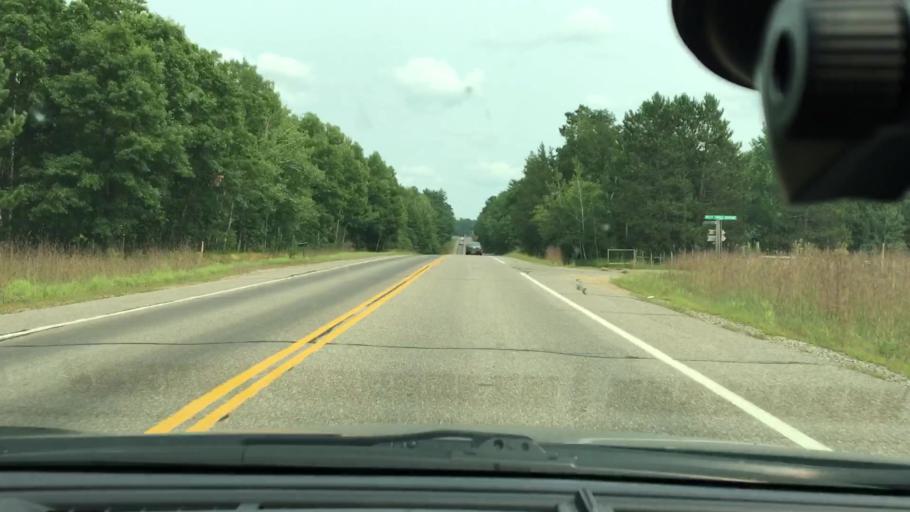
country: US
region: Minnesota
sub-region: Crow Wing County
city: Cross Lake
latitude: 46.7309
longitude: -93.9774
